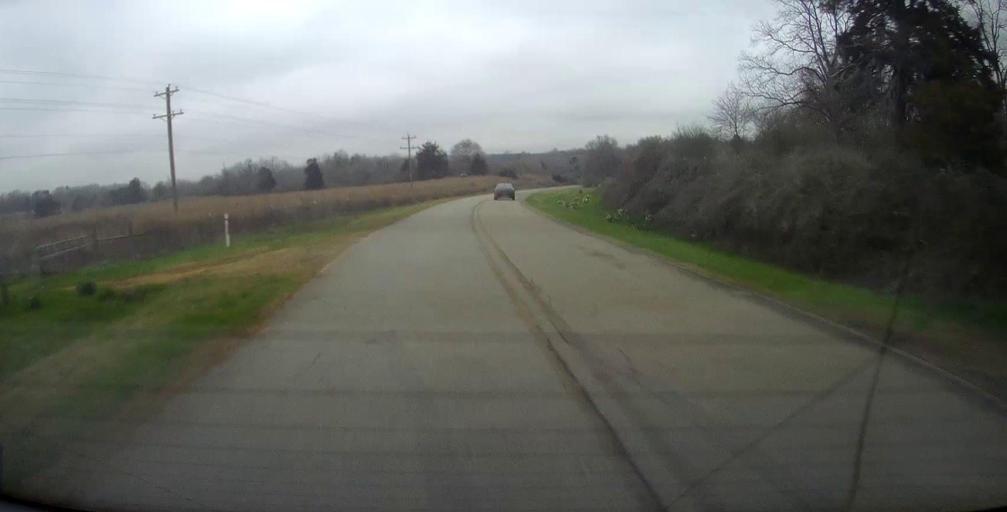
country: US
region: Georgia
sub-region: Lamar County
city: Barnesville
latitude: 33.0392
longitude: -84.1121
